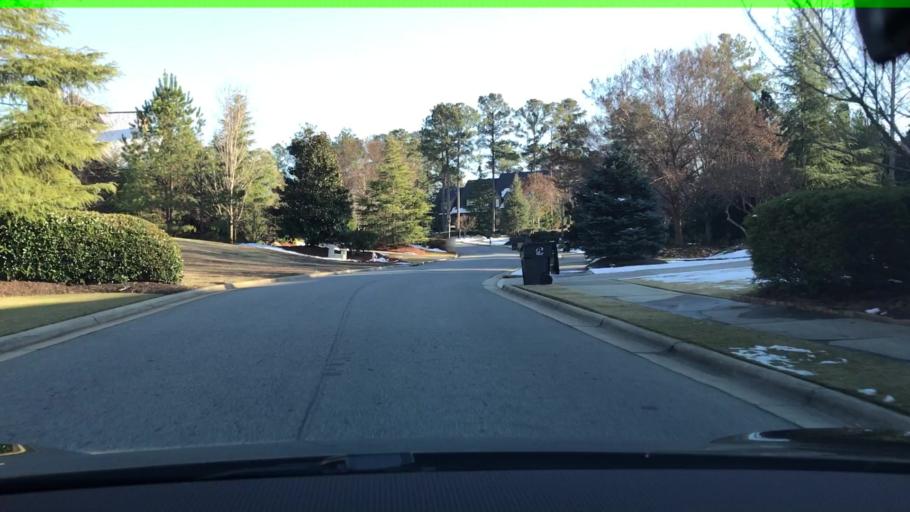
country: US
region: Georgia
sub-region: Gwinnett County
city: Suwanee
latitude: 34.0713
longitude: -84.0962
